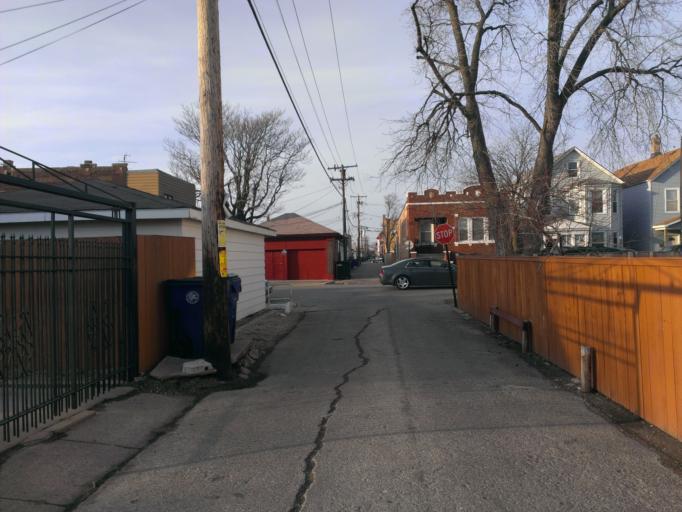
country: US
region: Illinois
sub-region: Cook County
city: Cicero
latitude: 41.8471
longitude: -87.7632
